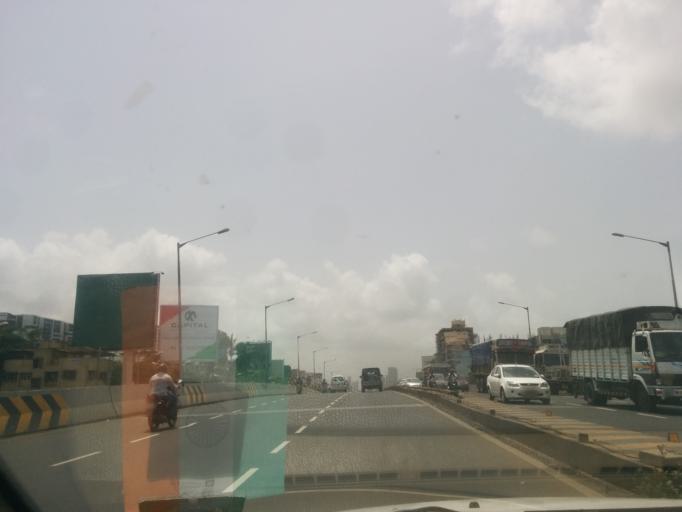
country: IN
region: Maharashtra
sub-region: Mumbai Suburban
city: Mumbai
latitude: 19.0618
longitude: 72.8465
